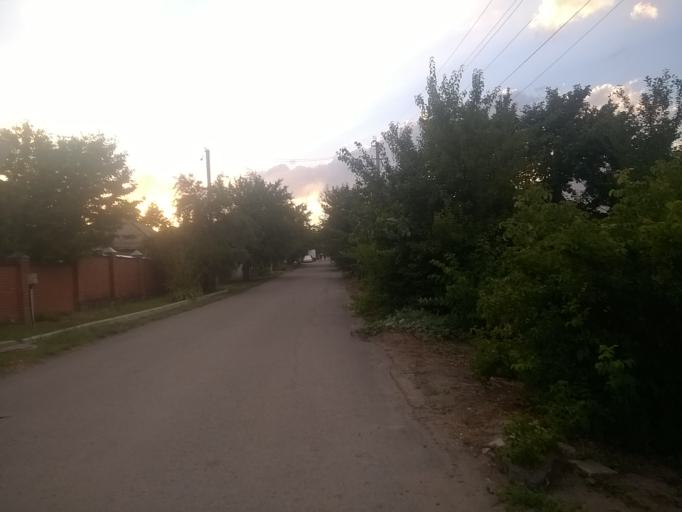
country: RU
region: Rostov
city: Donetsk
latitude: 48.3326
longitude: 39.9587
